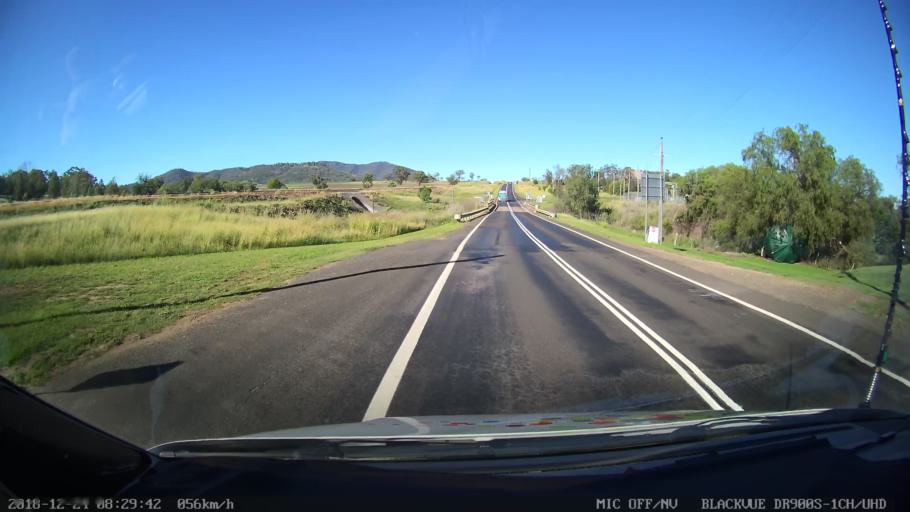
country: AU
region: New South Wales
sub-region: Tamworth Municipality
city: Phillip
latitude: -31.2642
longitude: 150.7319
